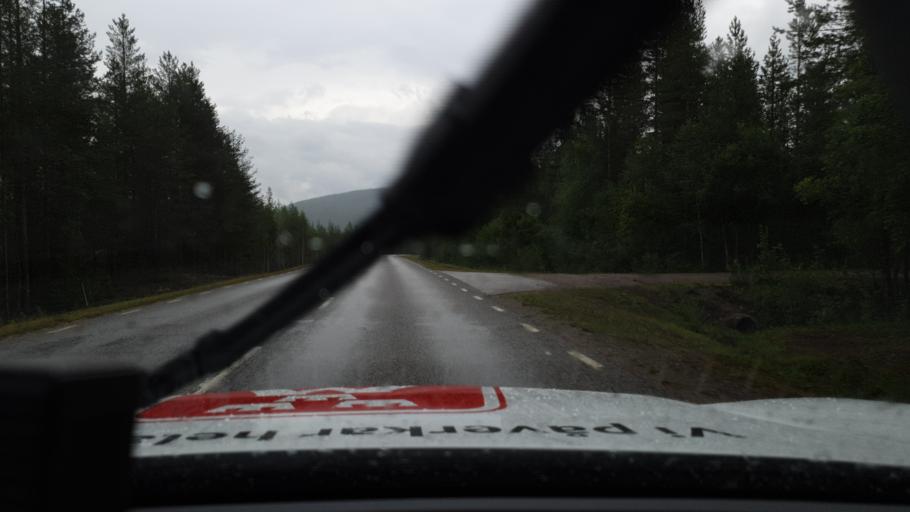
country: SE
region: Norrbotten
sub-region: Jokkmokks Kommun
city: Jokkmokk
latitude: 66.4658
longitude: 20.4479
